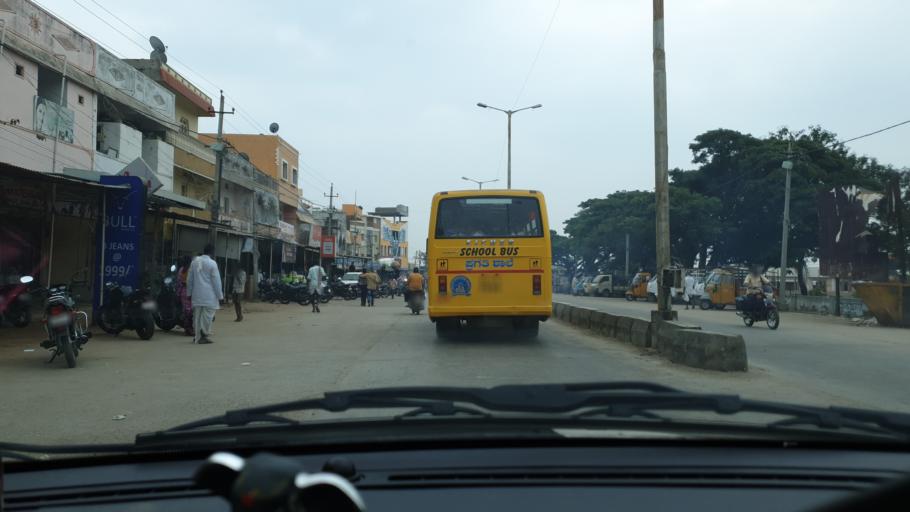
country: IN
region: Karnataka
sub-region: Yadgir
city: Gurmatkal
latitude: 16.8724
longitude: 77.3906
